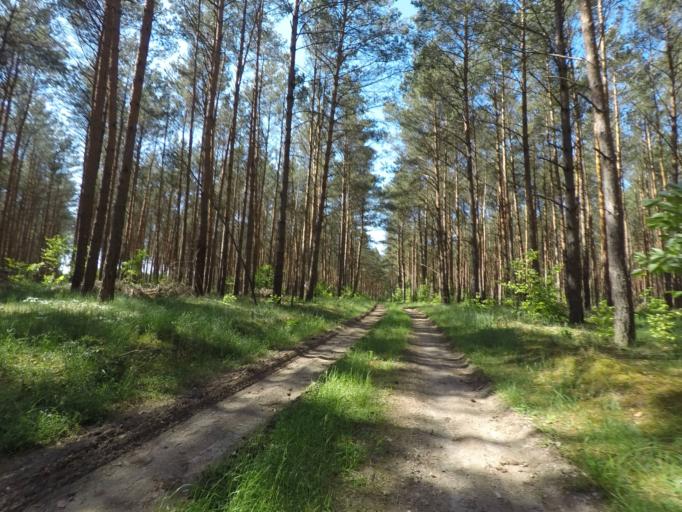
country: DE
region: Brandenburg
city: Melchow
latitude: 52.8210
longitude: 13.7539
